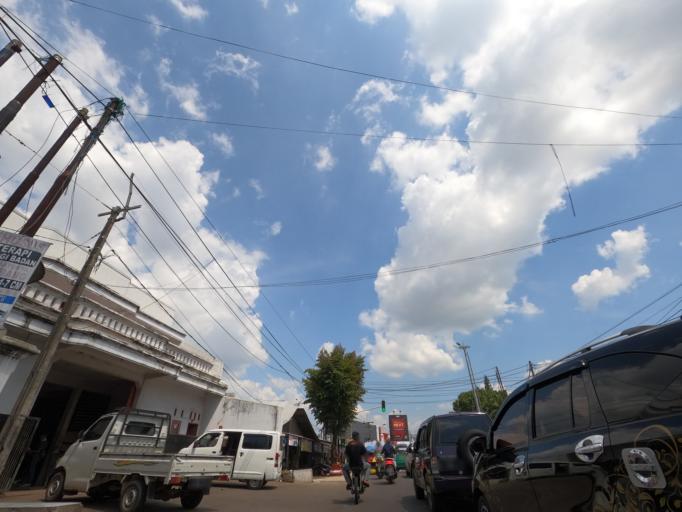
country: ID
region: West Java
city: Pamanukan
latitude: -6.5518
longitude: 107.7531
